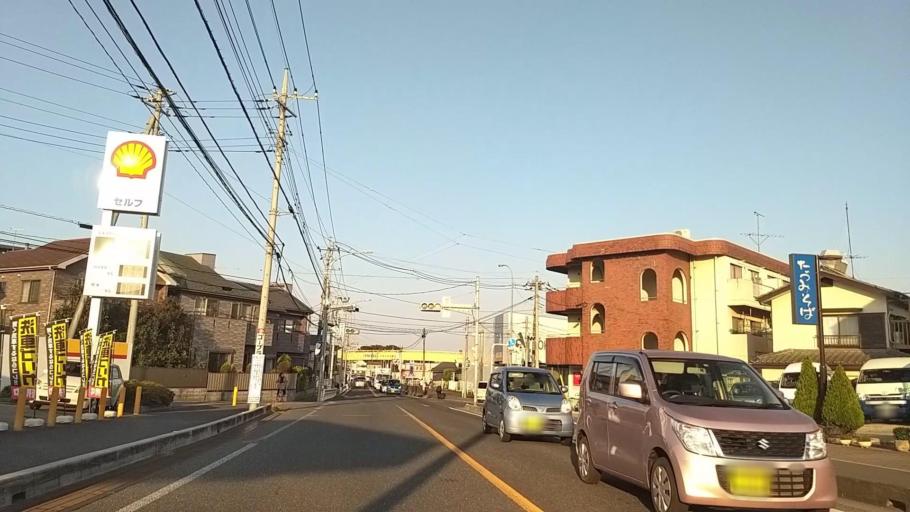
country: JP
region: Saitama
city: Tokorozawa
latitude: 35.8167
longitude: 139.4628
